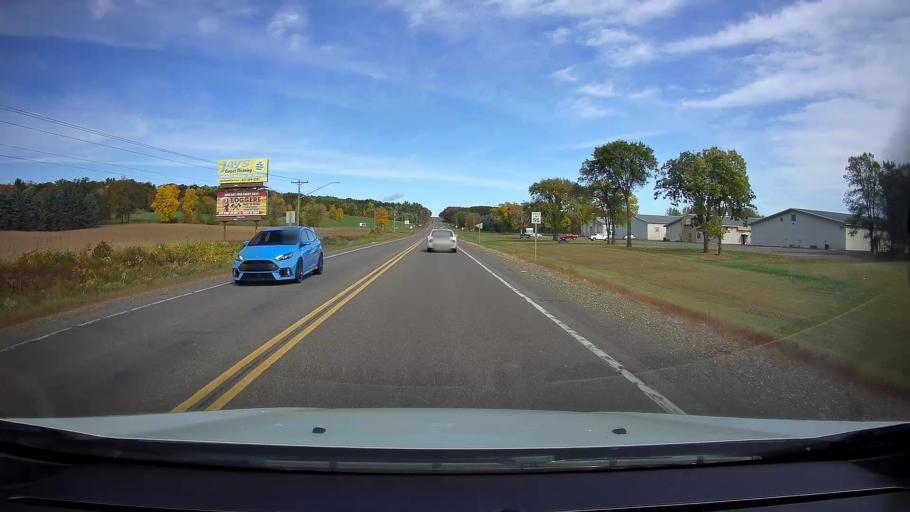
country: US
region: Wisconsin
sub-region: Polk County
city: Saint Croix Falls
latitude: 45.3628
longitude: -92.6366
